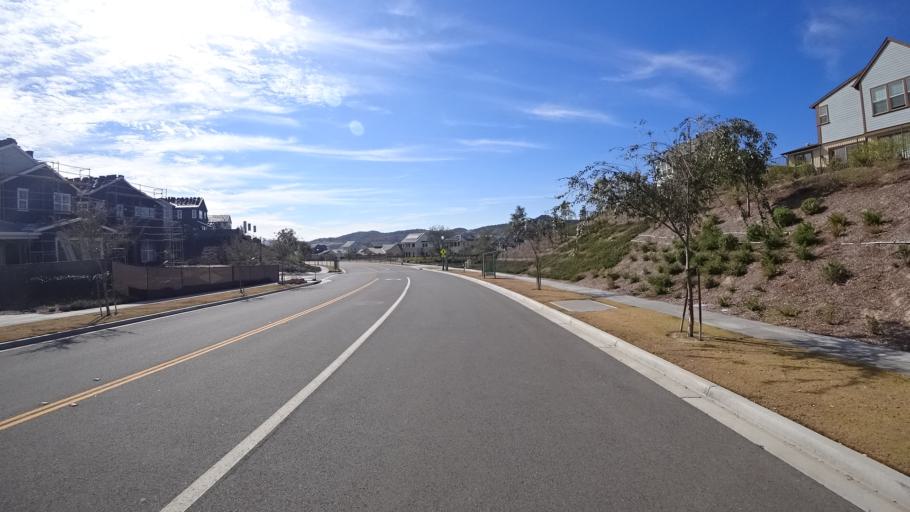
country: US
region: California
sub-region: Orange County
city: Ladera Ranch
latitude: 33.5534
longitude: -117.6016
